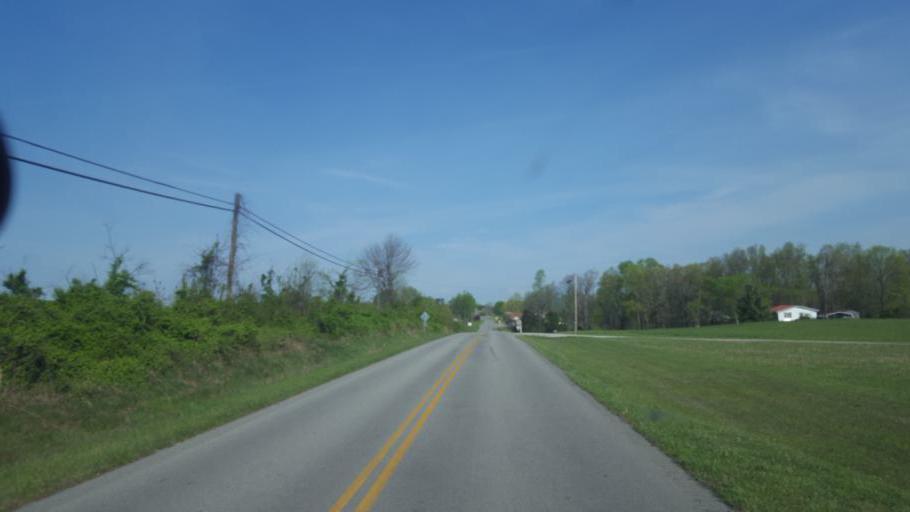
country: US
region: Kentucky
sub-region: Edmonson County
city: Brownsville
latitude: 37.2723
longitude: -86.1680
